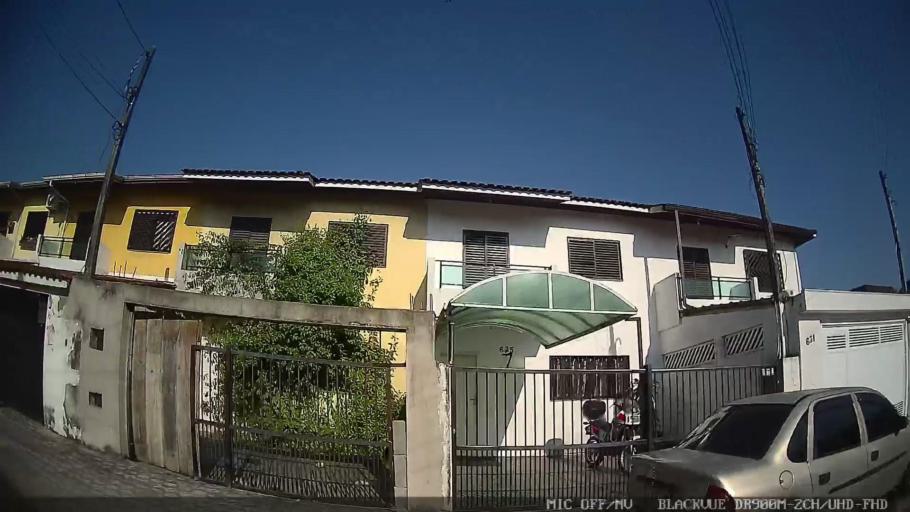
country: BR
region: Sao Paulo
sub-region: Guaruja
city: Guaruja
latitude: -23.9859
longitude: -46.2700
